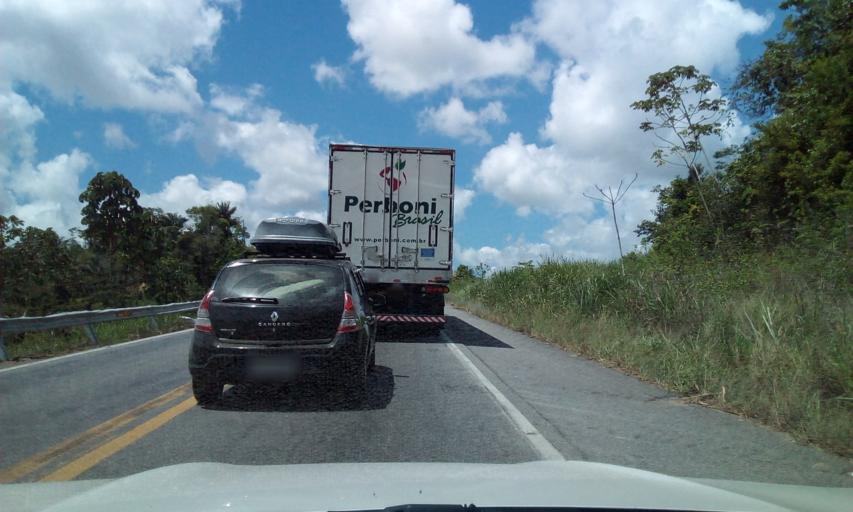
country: BR
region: Alagoas
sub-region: Sao Miguel Dos Campos
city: Sao Miguel dos Campos
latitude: -9.6872
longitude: -36.0362
